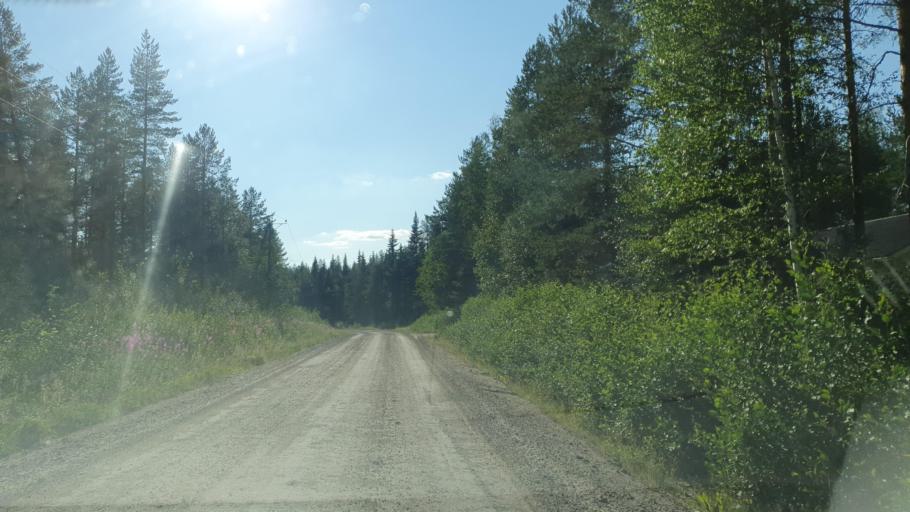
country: FI
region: Kainuu
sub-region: Kehys-Kainuu
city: Kuhmo
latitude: 64.0526
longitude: 29.5723
